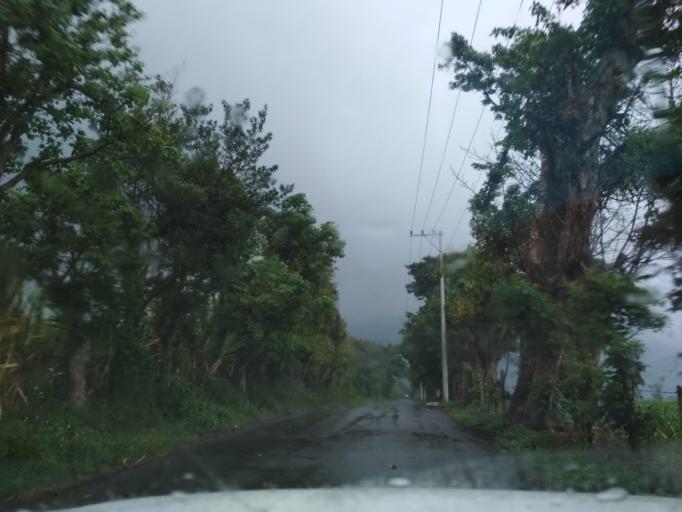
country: MX
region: Veracruz
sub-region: Mariano Escobedo
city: Chicola
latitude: 18.9036
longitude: -97.1171
